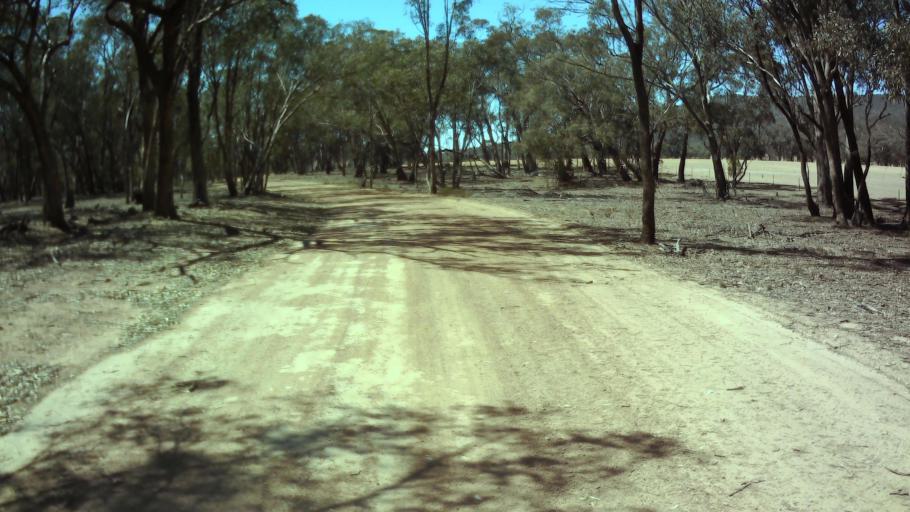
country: AU
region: New South Wales
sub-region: Weddin
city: Grenfell
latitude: -33.9645
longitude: 148.0898
